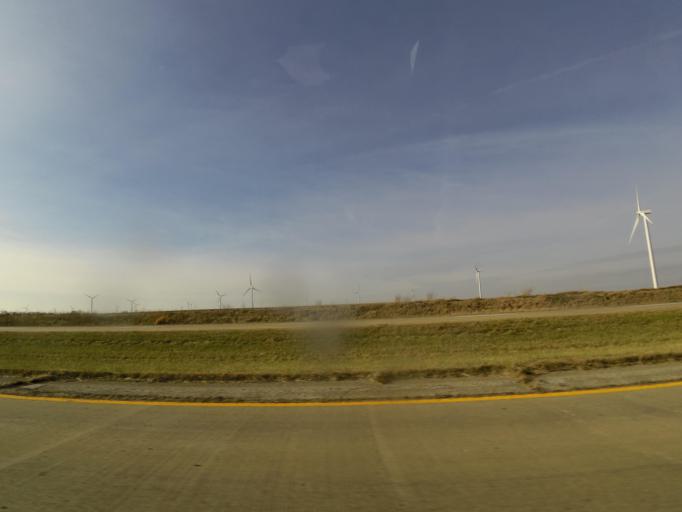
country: US
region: Illinois
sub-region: Macon County
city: Maroa
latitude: 40.0472
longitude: -88.9658
